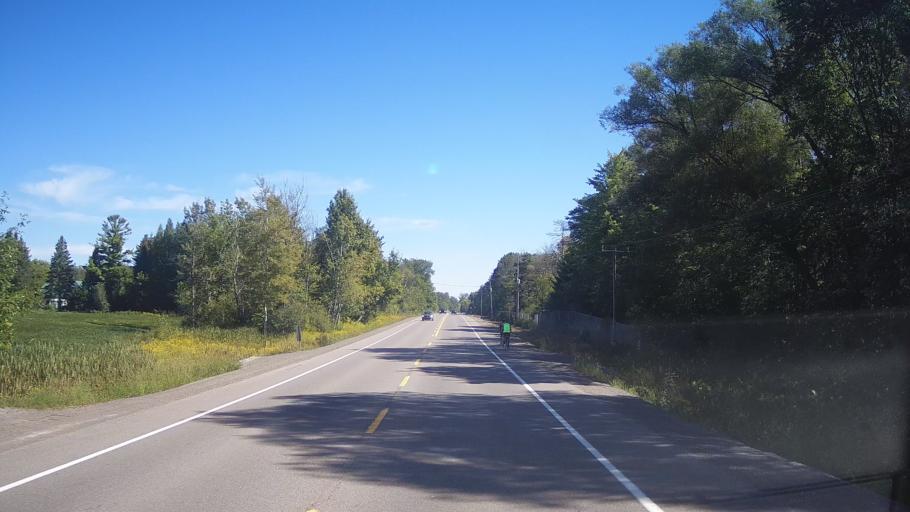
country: CA
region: Ontario
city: Bells Corners
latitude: 45.0572
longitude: -75.6775
